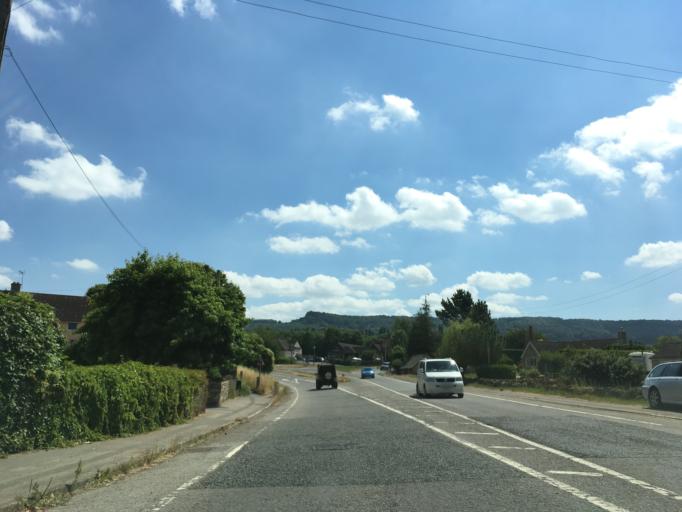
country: GB
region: England
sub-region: Gloucestershire
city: Shurdington
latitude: 51.8402
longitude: -2.1425
